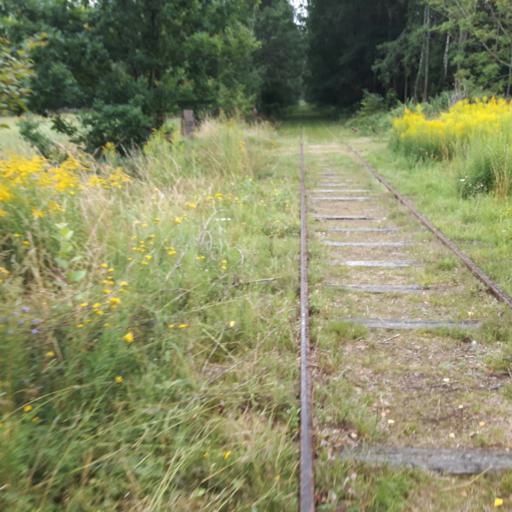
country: SE
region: Skane
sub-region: Ostra Goinge Kommun
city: Broby
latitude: 56.2634
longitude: 14.0712
